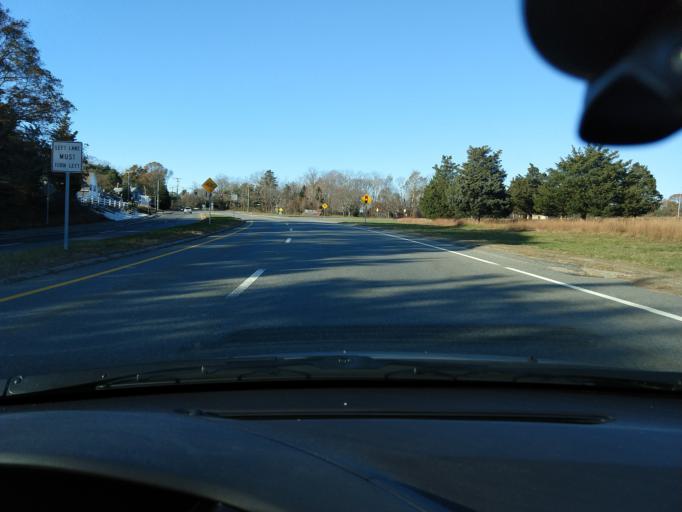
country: US
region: Massachusetts
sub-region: Barnstable County
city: Eastham
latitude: 41.8366
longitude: -69.9740
